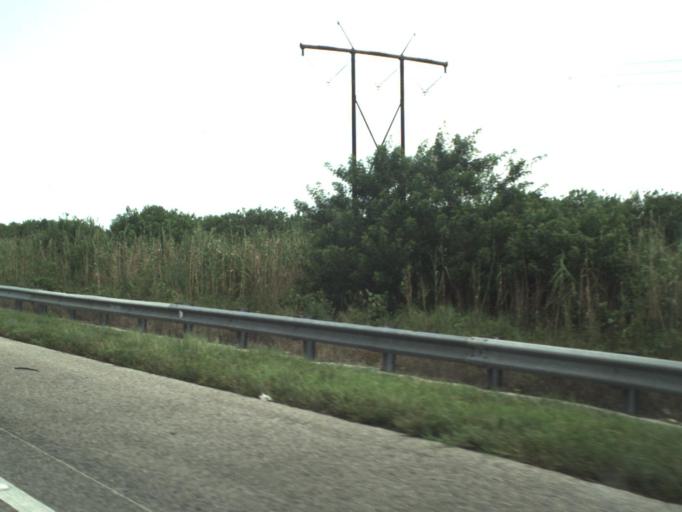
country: US
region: Florida
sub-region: Broward County
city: Weston
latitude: 26.3097
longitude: -80.5182
